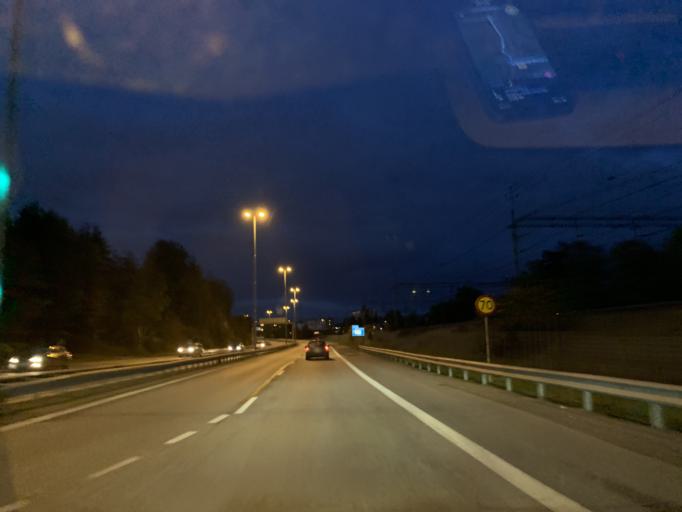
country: SE
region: Stockholm
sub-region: Huddinge Kommun
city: Huddinge
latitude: 59.2318
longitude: 17.9692
